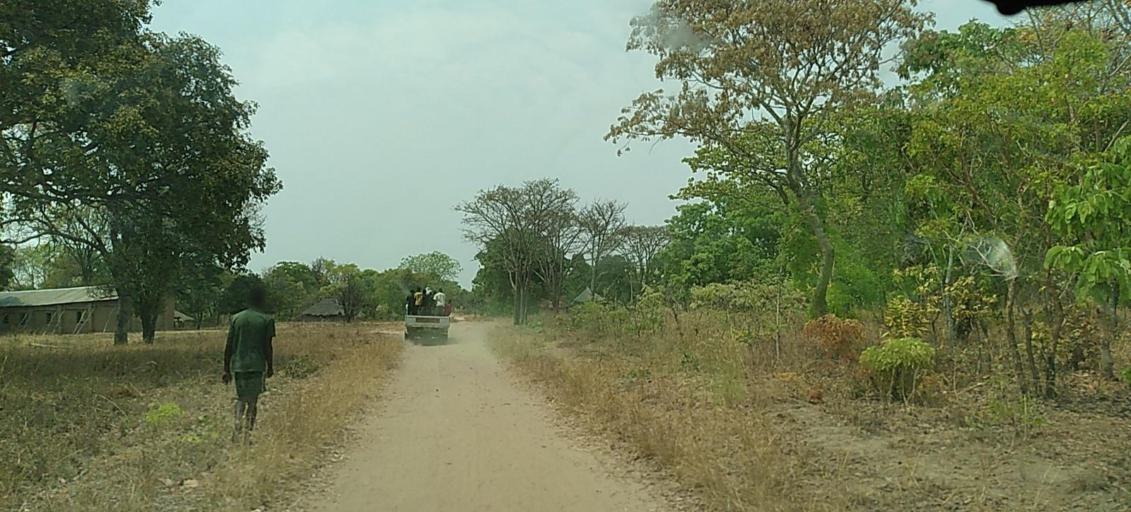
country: ZM
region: North-Western
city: Kabompo
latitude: -13.4832
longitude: 24.4600
